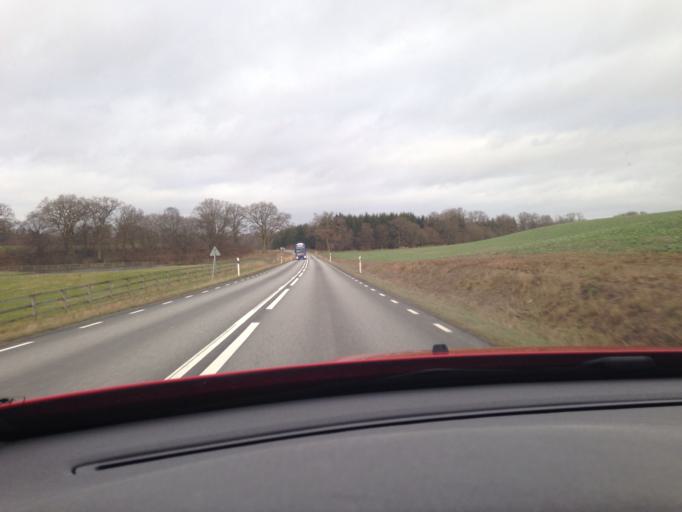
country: SE
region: Skane
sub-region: Ystads Kommun
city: Ystad
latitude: 55.5244
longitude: 13.7764
